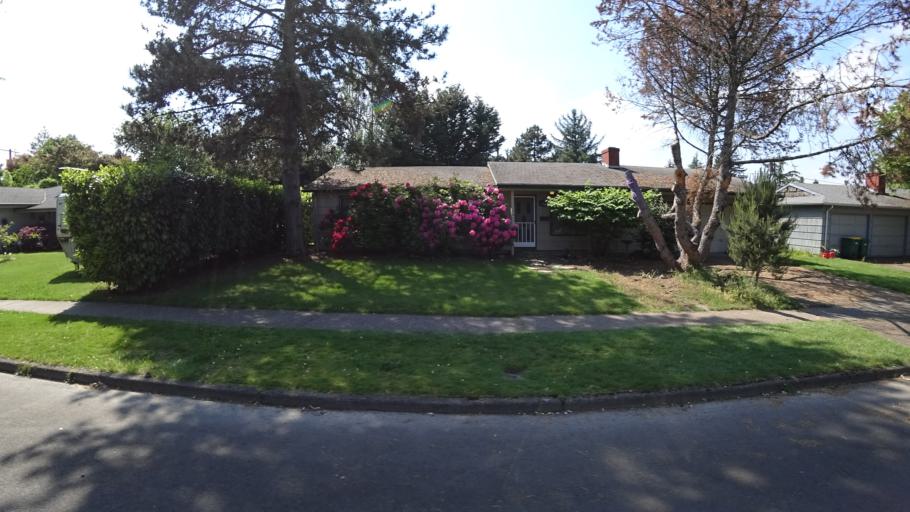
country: US
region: Oregon
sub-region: Washington County
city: Beaverton
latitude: 45.4711
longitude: -122.7945
